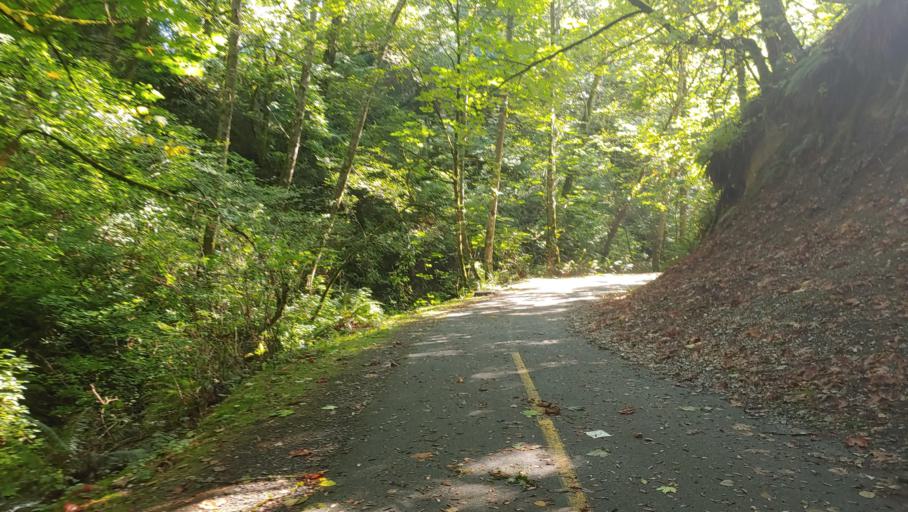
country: US
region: Washington
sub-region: King County
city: Des Moines
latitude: 47.4143
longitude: -122.3087
